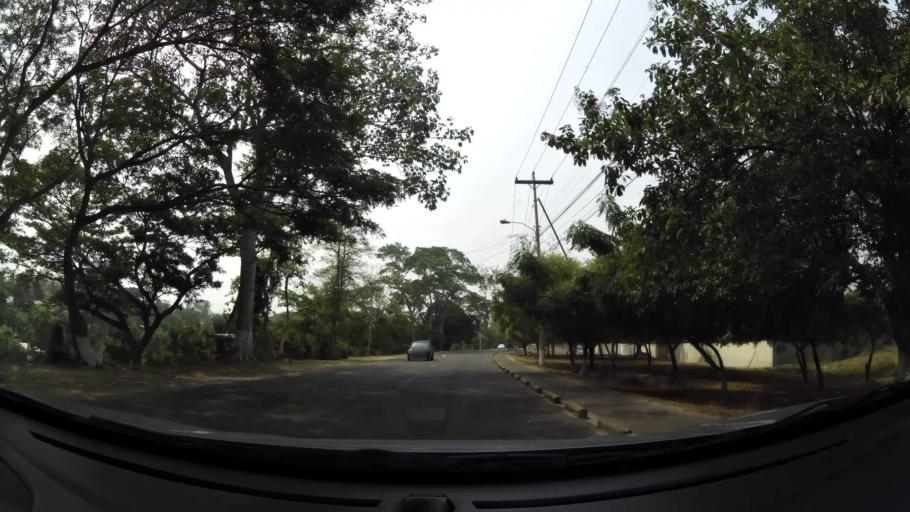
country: HN
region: Cortes
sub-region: San Pedro Sula
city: Pena Blanca
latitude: 15.5538
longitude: -88.0127
